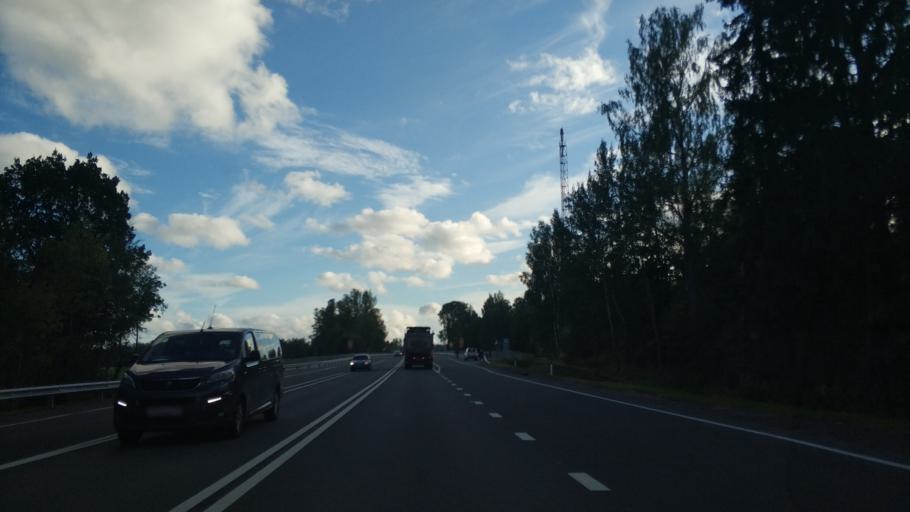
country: RU
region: Leningrad
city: Priozersk
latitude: 60.8535
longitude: 30.1510
